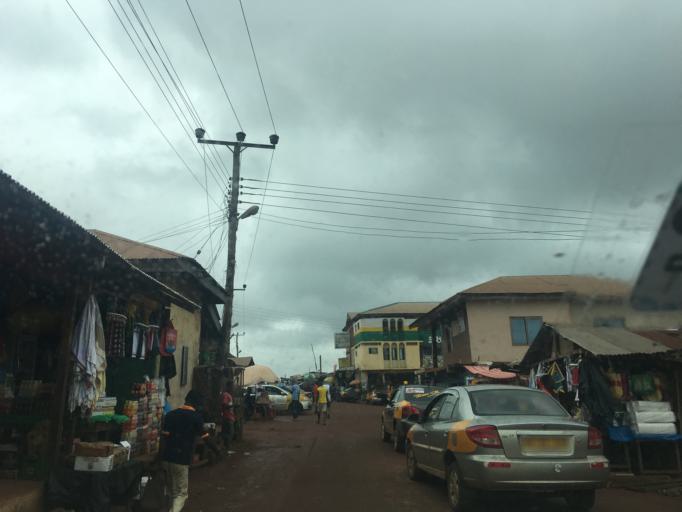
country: GH
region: Western
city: Wassa-Akropong
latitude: 5.8092
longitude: -2.4361
